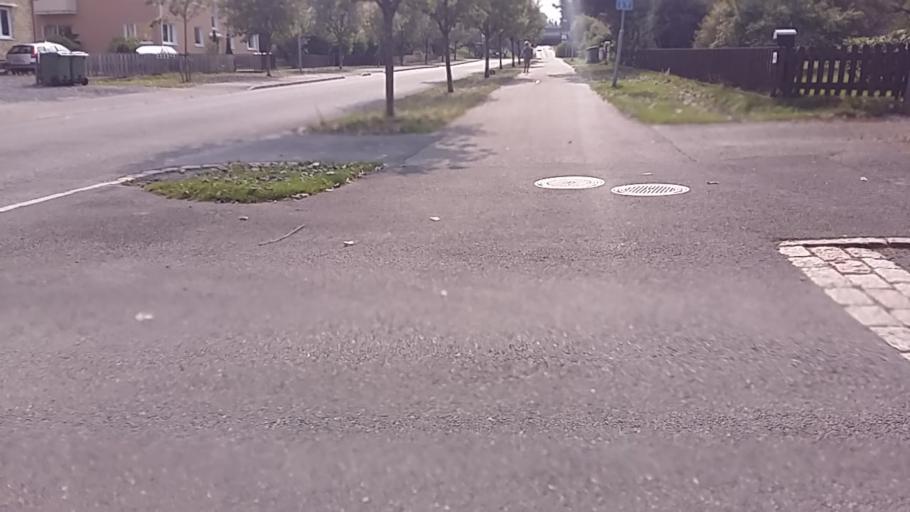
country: SE
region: Joenkoeping
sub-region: Jonkopings Kommun
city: Jonkoping
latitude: 57.7605
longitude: 14.1523
